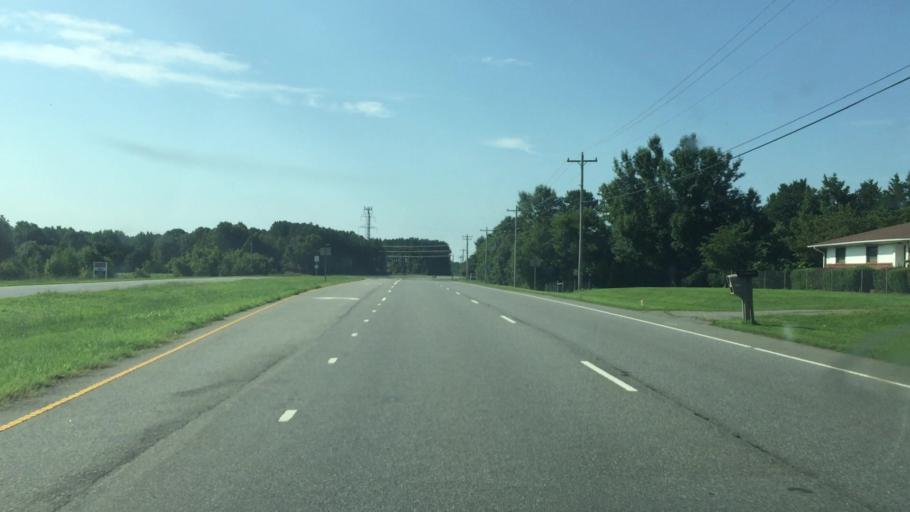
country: US
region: North Carolina
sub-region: Cabarrus County
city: Kannapolis
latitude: 35.4756
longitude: -80.6724
